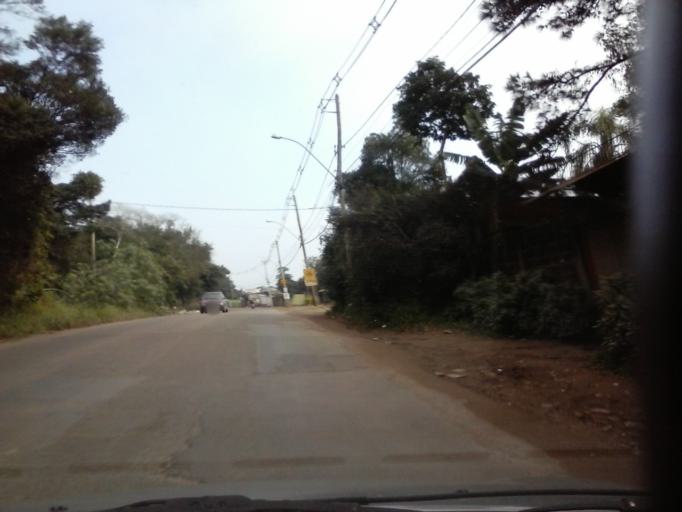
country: BR
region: Rio Grande do Sul
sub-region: Viamao
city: Viamao
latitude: -30.0506
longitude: -51.0664
